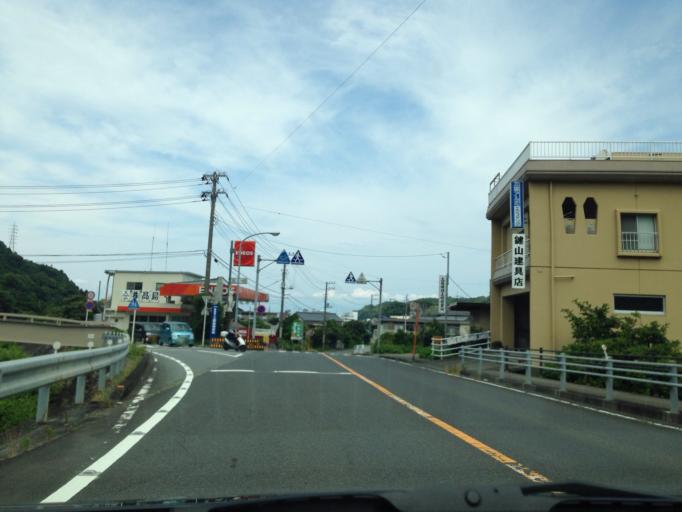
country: JP
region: Shizuoka
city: Heda
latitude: 34.9070
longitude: 138.8023
